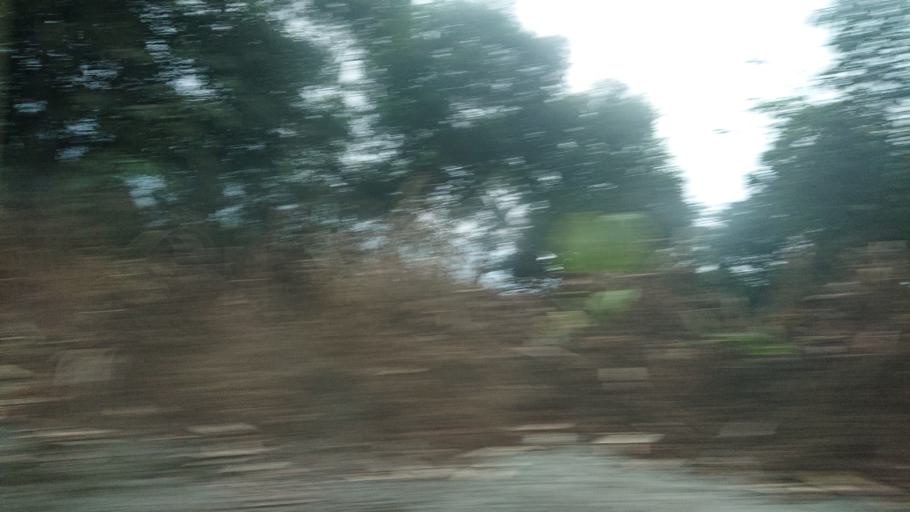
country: TW
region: Taiwan
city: Lugu
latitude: 23.5940
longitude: 120.7173
